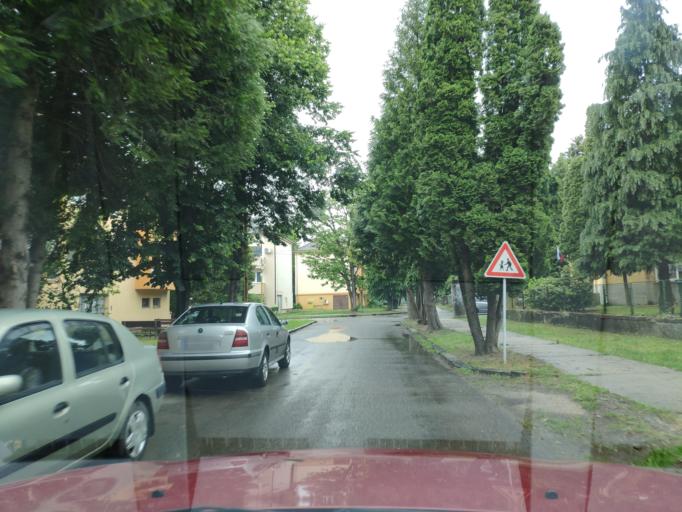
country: SK
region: Kosicky
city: Cierna nad Tisou
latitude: 48.4154
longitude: 22.0891
